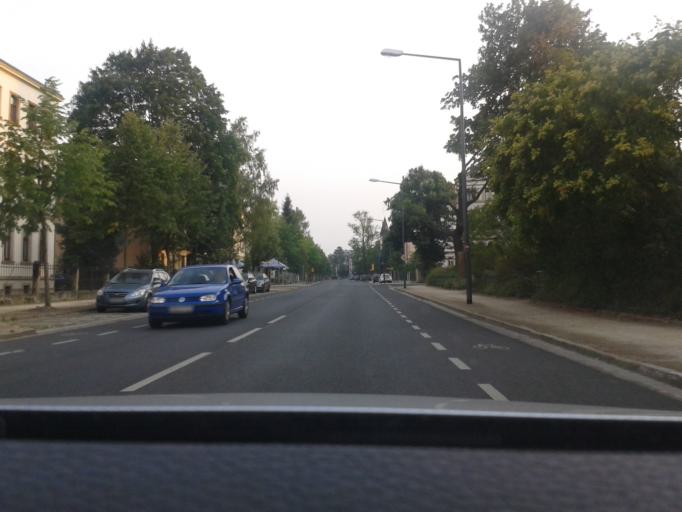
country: DE
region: Saxony
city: Albertstadt
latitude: 51.0445
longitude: 13.8078
